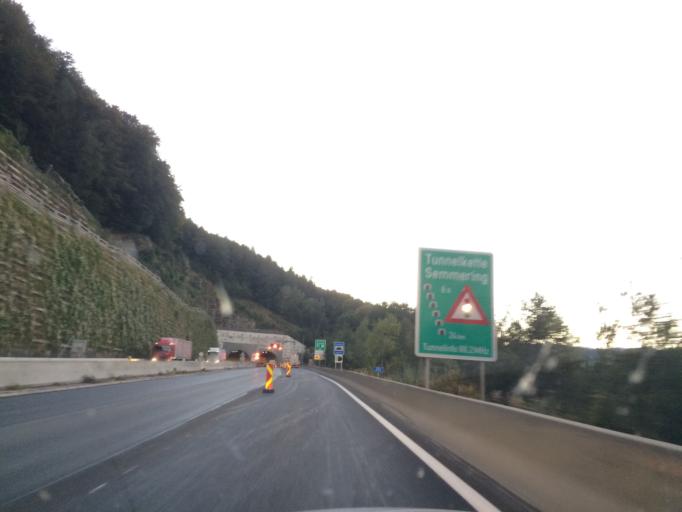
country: AT
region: Lower Austria
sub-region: Politischer Bezirk Neunkirchen
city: Schottwien
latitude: 47.6551
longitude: 15.8838
